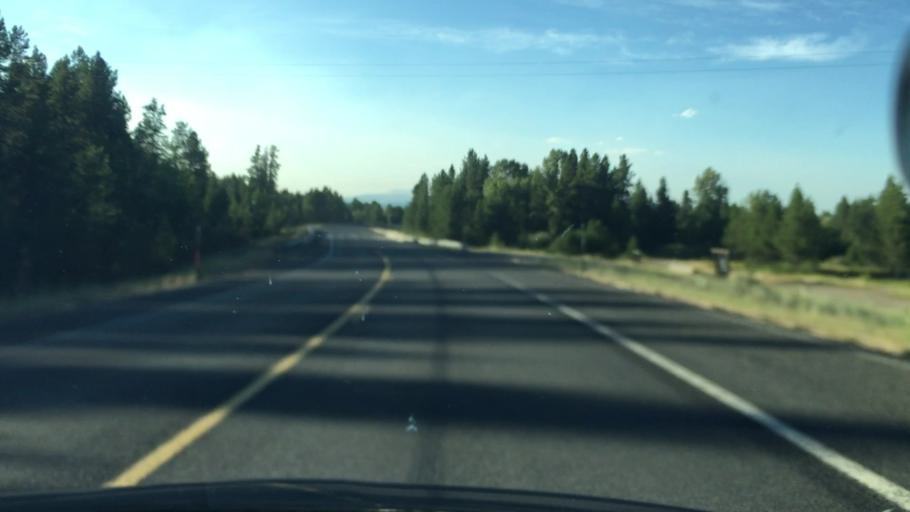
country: US
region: Idaho
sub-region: Valley County
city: McCall
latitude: 44.7876
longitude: -116.0766
